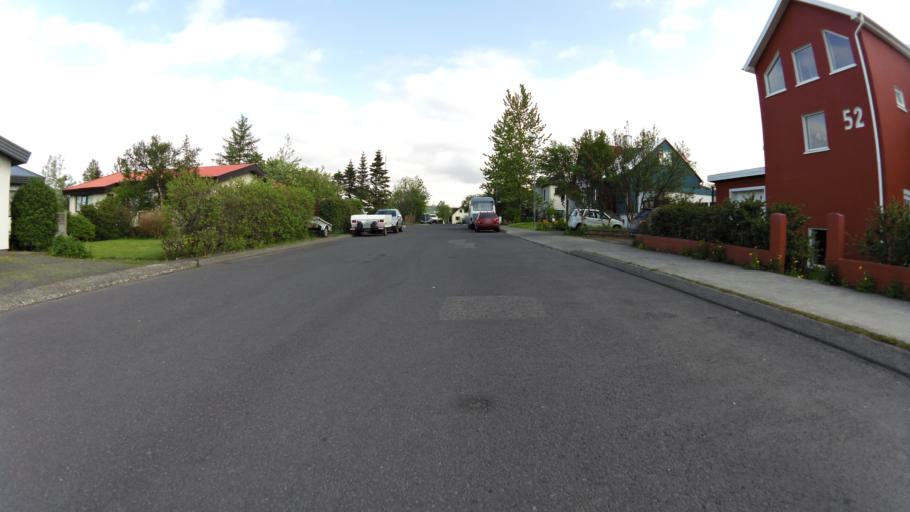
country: IS
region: Capital Region
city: Reykjavik
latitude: 64.1250
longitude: -21.8564
